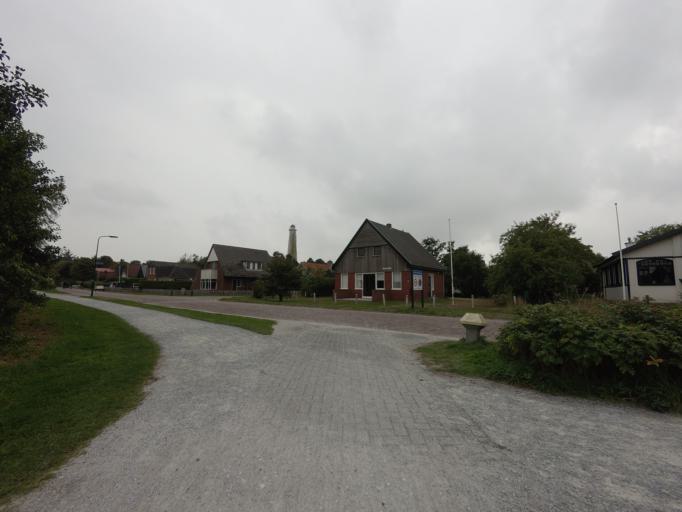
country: NL
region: Friesland
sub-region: Gemeente Schiermonnikoog
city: Schiermonnikoog
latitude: 53.4831
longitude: 6.1593
